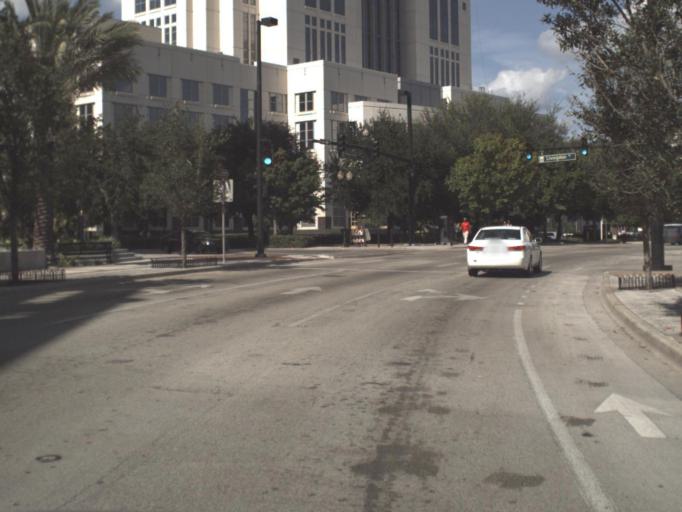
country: US
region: Florida
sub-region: Orange County
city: Orlando
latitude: 28.5472
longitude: -81.3765
